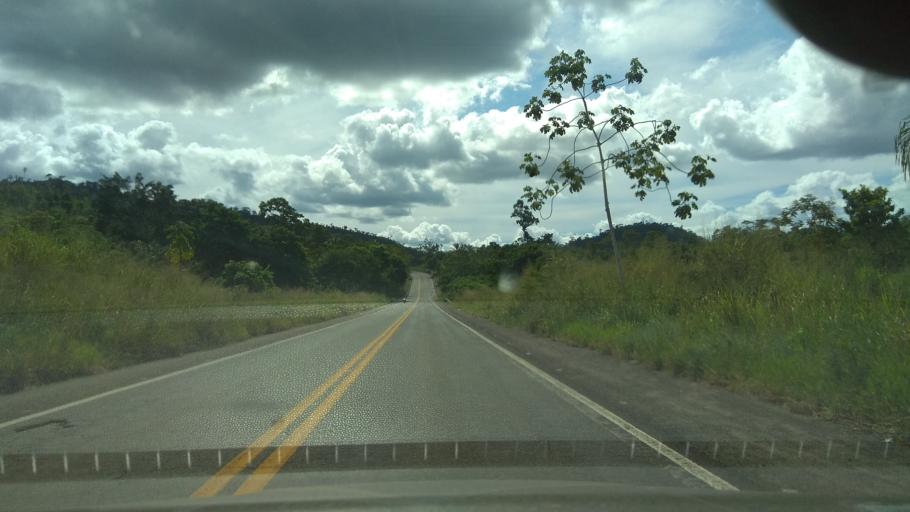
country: BR
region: Bahia
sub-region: Ubaitaba
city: Ubaitaba
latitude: -14.2499
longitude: -39.3571
